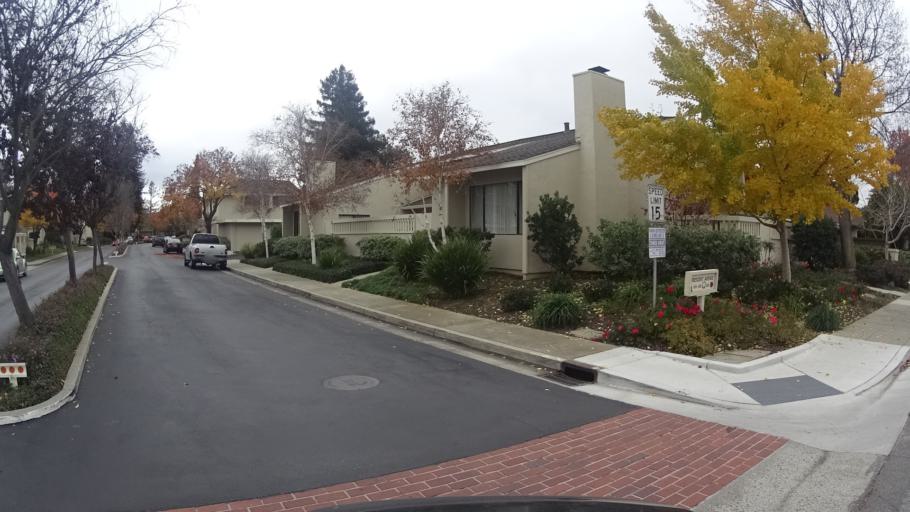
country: US
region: California
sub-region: Santa Clara County
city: Sunnyvale
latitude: 37.3550
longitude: -122.0254
